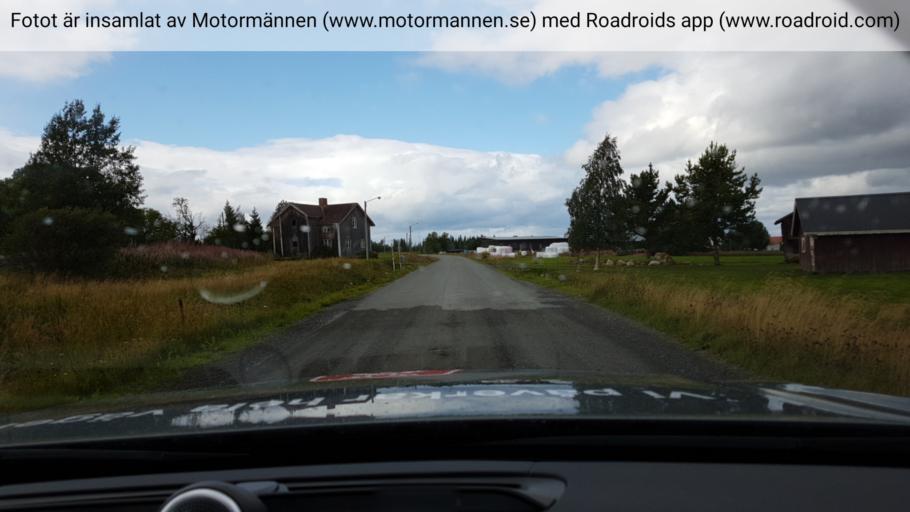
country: SE
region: Jaemtland
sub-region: OEstersunds Kommun
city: Lit
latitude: 63.6817
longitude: 14.8563
